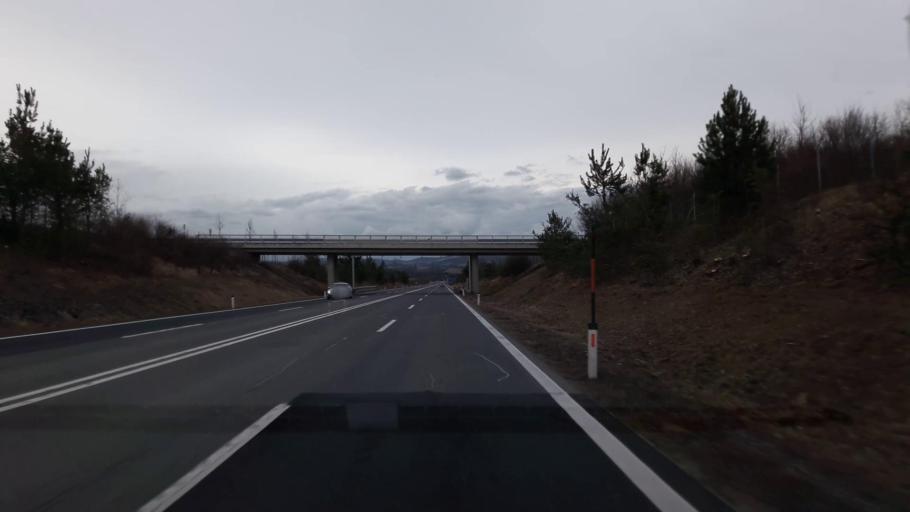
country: AT
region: Burgenland
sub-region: Politischer Bezirk Oberpullendorf
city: Markt Sankt Martin
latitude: 47.5551
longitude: 16.4181
